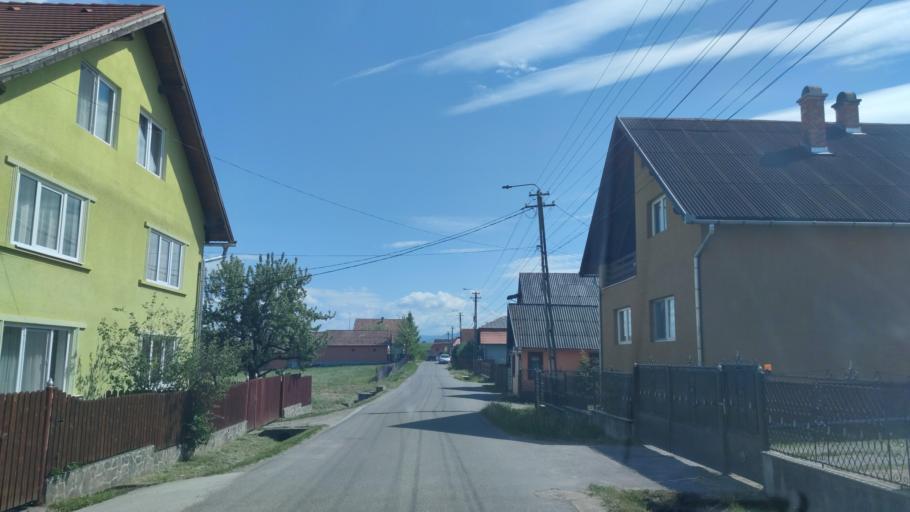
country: RO
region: Harghita
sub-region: Comuna Remetea
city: Remetea
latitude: 46.8027
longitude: 25.4529
